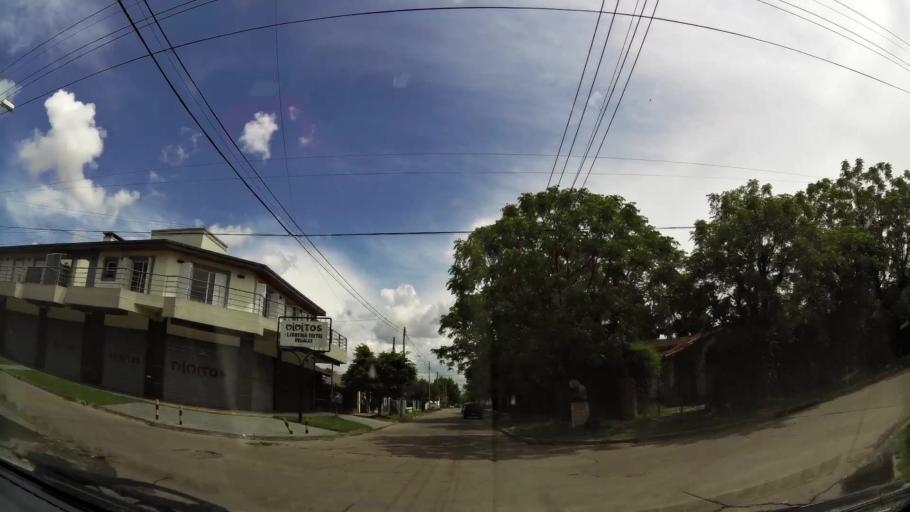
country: AR
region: Buenos Aires
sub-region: Partido de Quilmes
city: Quilmes
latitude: -34.7785
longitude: -58.2695
